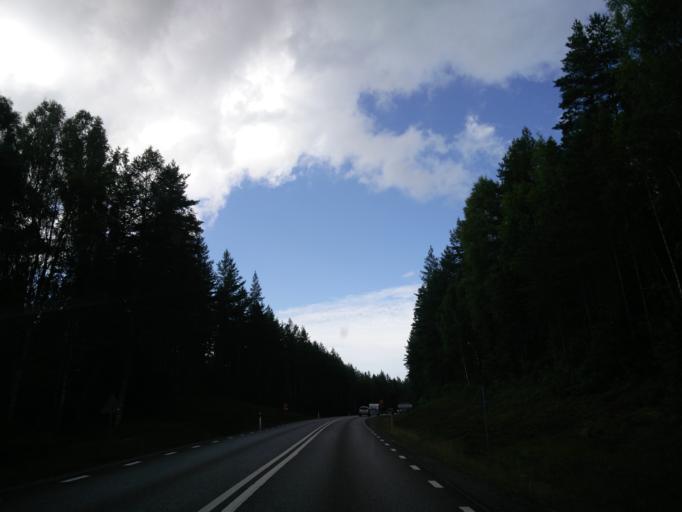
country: SE
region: Vaermland
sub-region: Hagfors Kommun
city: Ekshaerad
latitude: 60.4266
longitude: 13.2565
